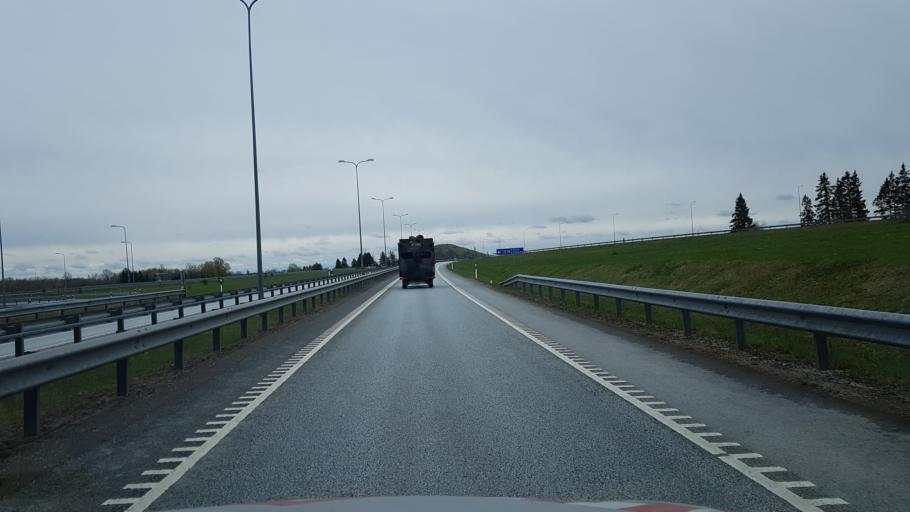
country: EE
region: Ida-Virumaa
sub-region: Kohtla-Jaerve linn
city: Kohtla-Jarve
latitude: 59.4036
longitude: 27.3268
